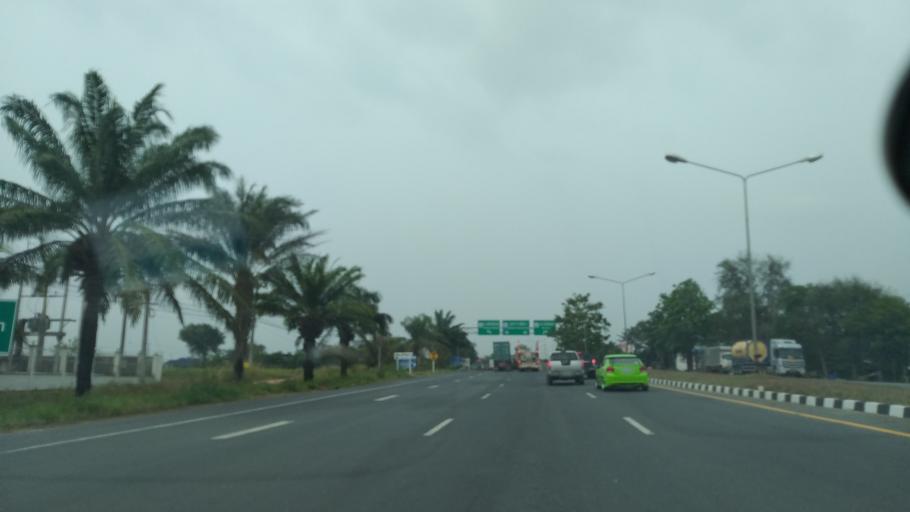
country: TH
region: Chon Buri
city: Ko Chan
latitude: 13.3218
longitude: 101.2695
